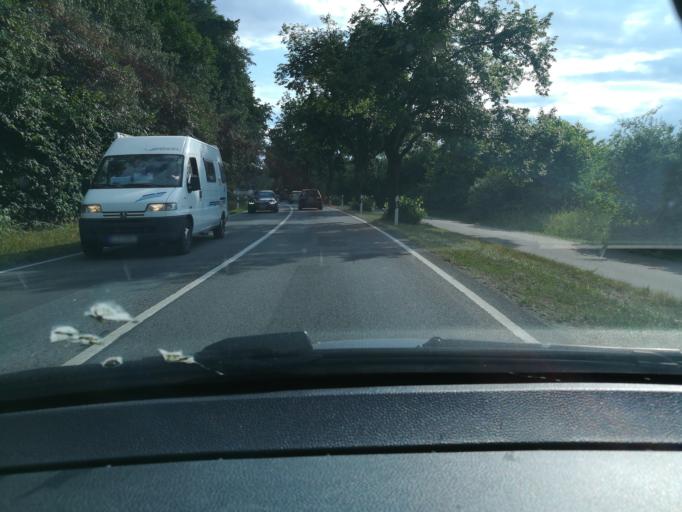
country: DE
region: Mecklenburg-Vorpommern
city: Waren
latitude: 53.5161
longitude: 12.6458
